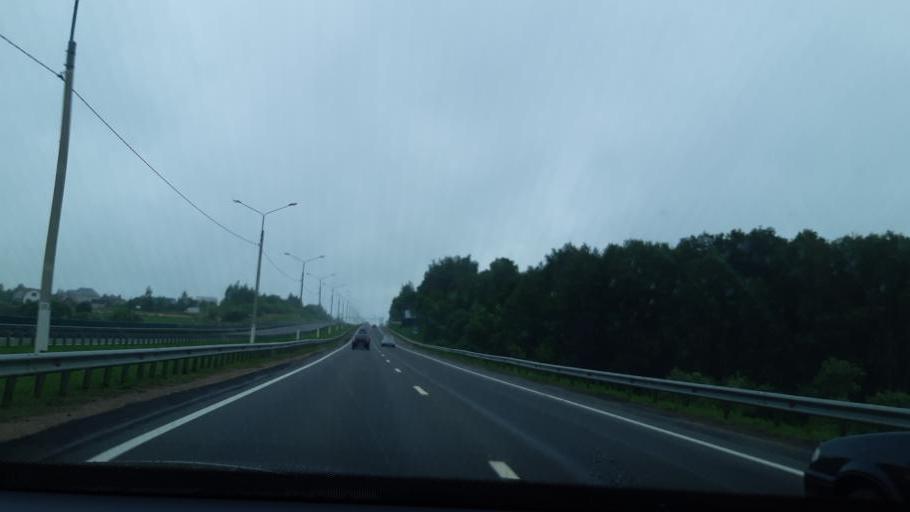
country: RU
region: Smolensk
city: Talashkino
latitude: 54.6766
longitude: 32.1445
